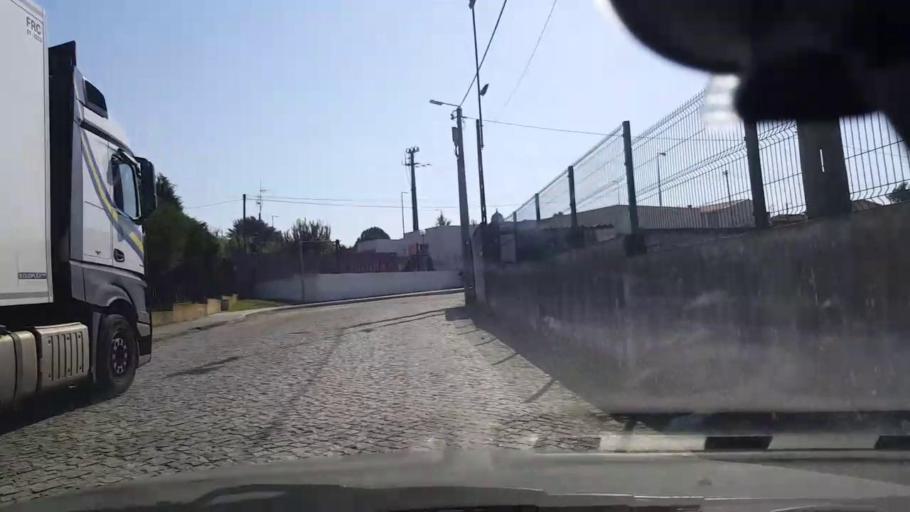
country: PT
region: Porto
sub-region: Vila do Conde
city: Arvore
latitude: 41.3804
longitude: -8.6821
